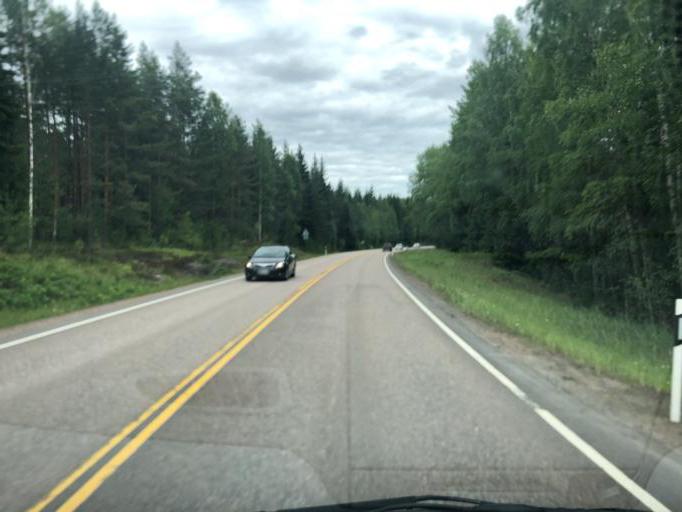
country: FI
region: Southern Savonia
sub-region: Mikkeli
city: Maentyharju
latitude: 61.1404
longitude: 27.1073
